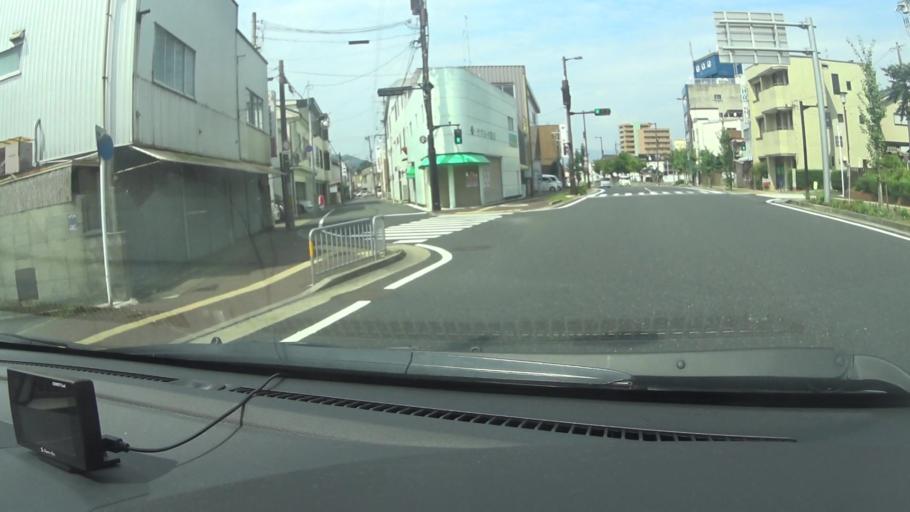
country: JP
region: Kyoto
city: Ayabe
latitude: 35.3020
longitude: 135.2418
